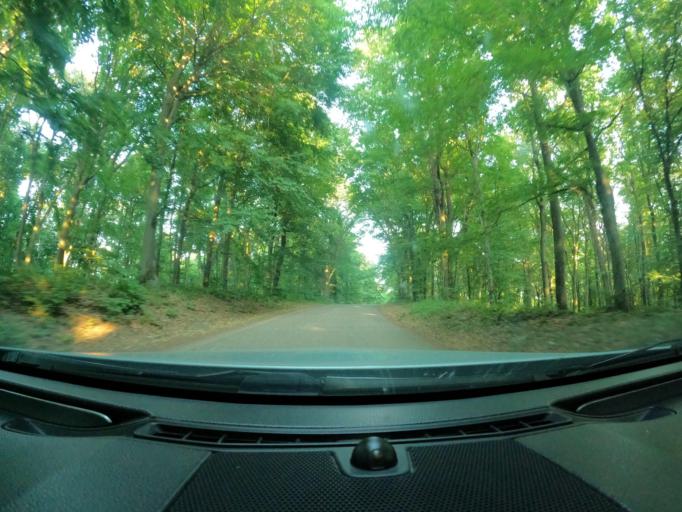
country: RS
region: Autonomna Pokrajina Vojvodina
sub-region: Juznobacki Okrug
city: Beocin
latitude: 45.1548
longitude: 19.7243
